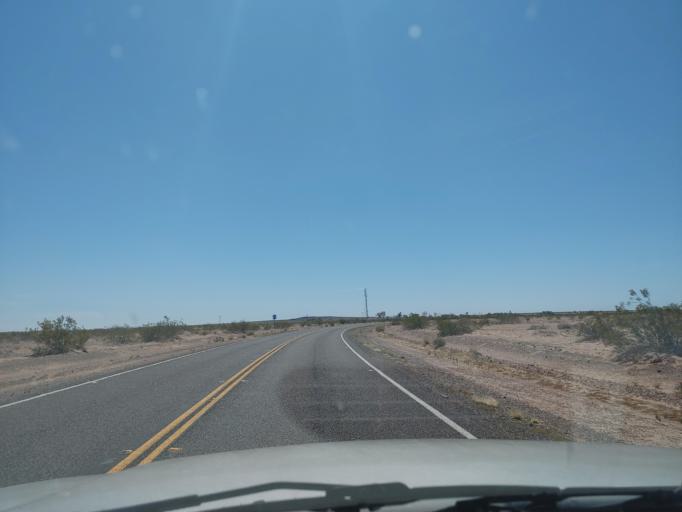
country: US
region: Arizona
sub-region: Maricopa County
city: Gila Bend
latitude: 32.8716
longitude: -113.2137
